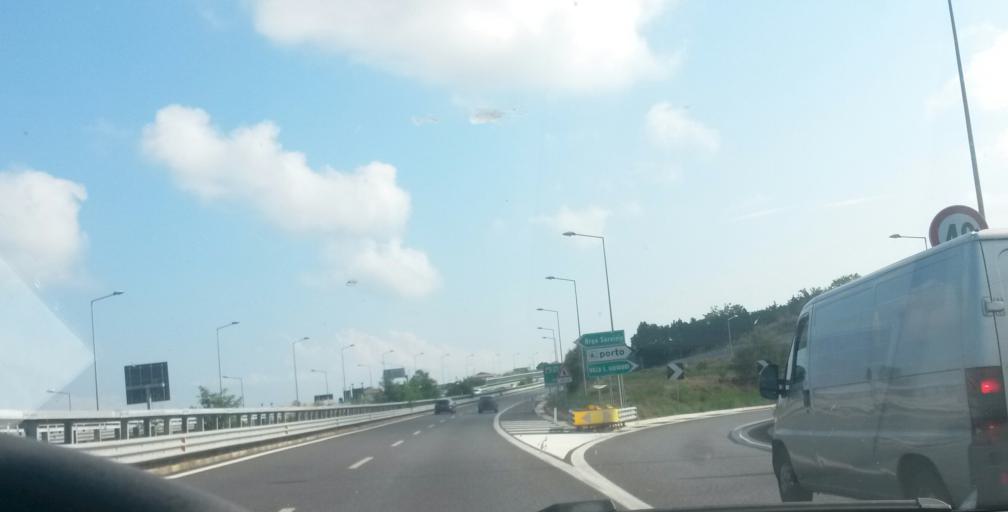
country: IT
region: Calabria
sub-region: Provincia di Reggio Calabria
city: Campo Calabro
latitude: 38.2046
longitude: 15.6407
